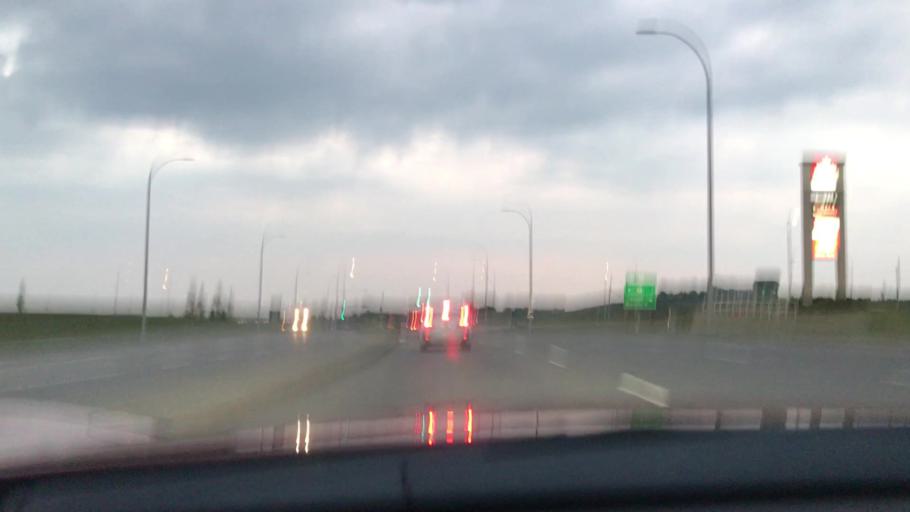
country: CA
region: Alberta
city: Airdrie
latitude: 51.2099
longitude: -113.9904
